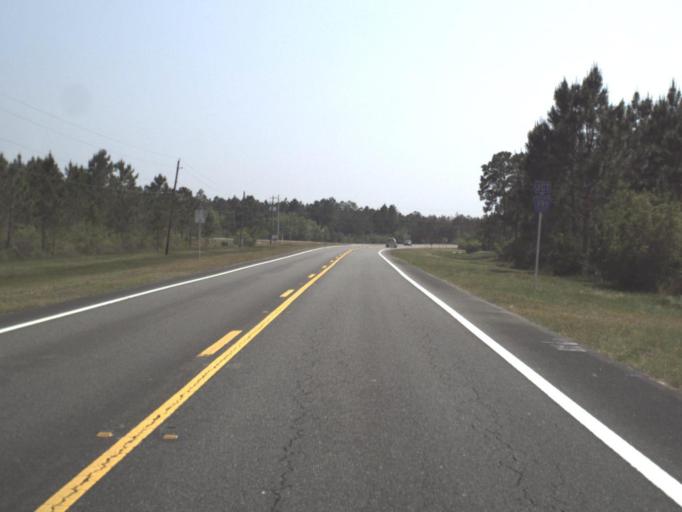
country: US
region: Florida
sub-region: Santa Rosa County
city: Tiger Point
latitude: 30.4806
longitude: -87.0793
